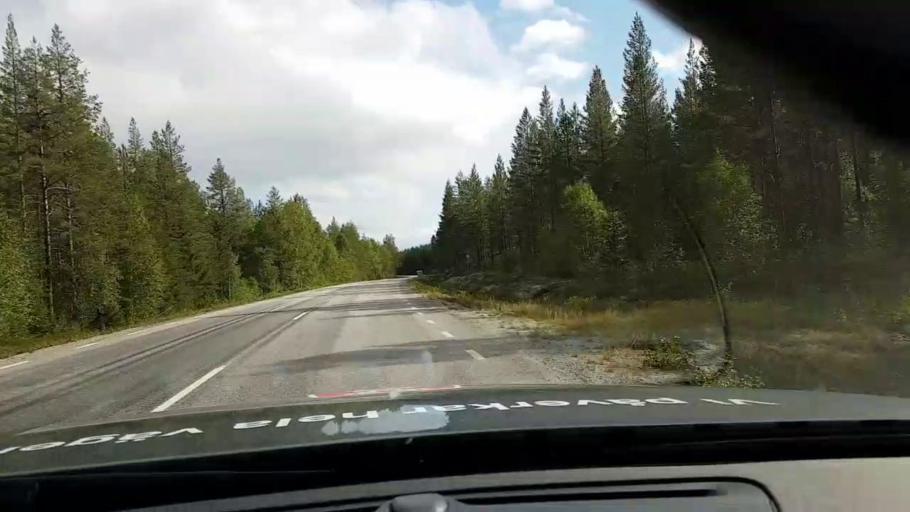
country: SE
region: Vaesternorrland
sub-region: OErnskoeldsviks Kommun
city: Bredbyn
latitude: 63.6395
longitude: 17.9009
